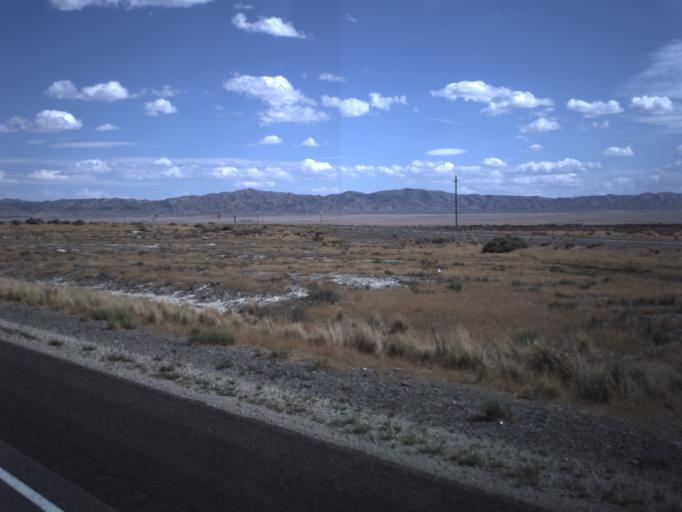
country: US
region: Utah
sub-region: Tooele County
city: Grantsville
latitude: 40.7305
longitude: -113.1172
